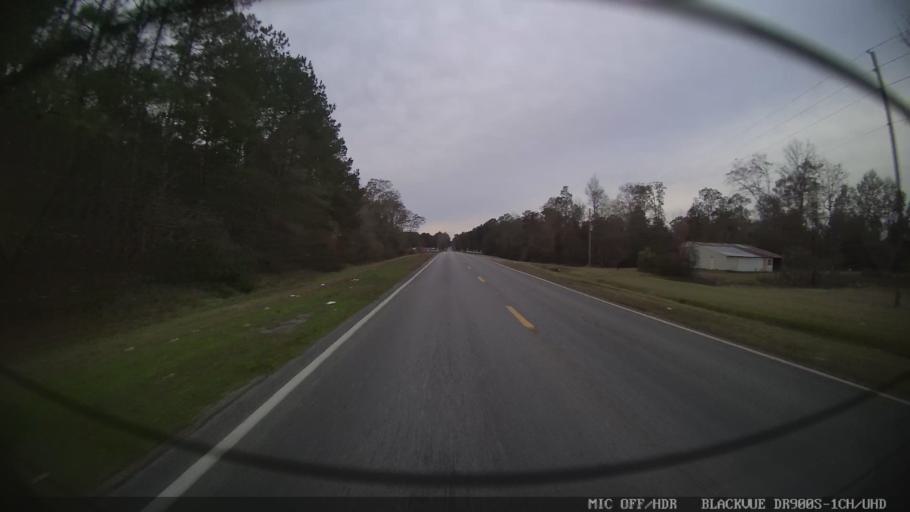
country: US
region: Mississippi
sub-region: Clarke County
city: Quitman
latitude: 32.0290
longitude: -88.8031
